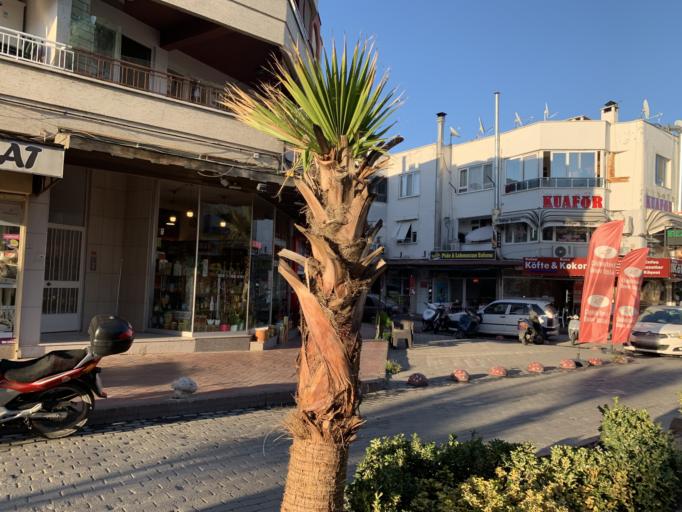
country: TR
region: Balikesir
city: Altinoluk
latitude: 39.5673
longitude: 26.7461
